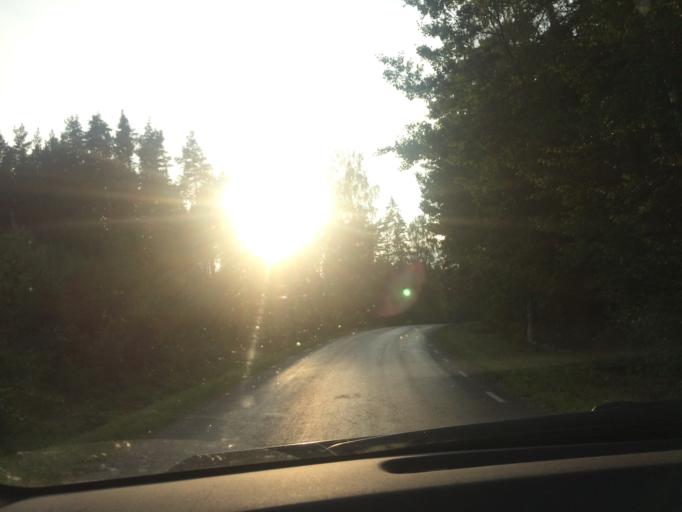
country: SE
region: Vaestra Goetaland
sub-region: Alingsas Kommun
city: Alingsas
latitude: 57.9908
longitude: 12.4624
